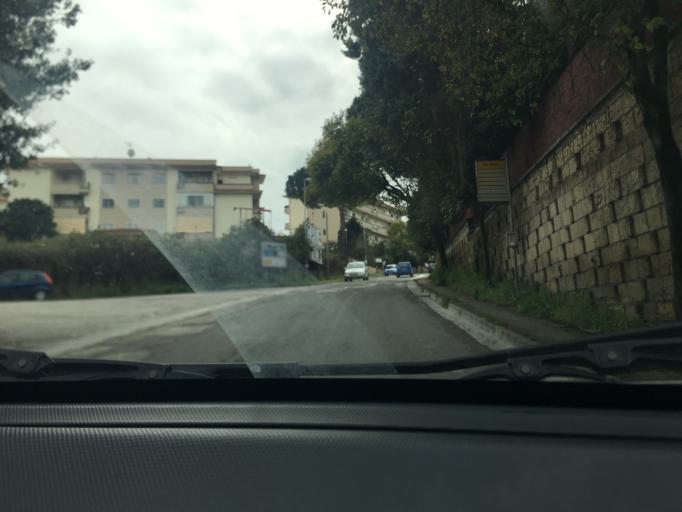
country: IT
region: Campania
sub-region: Provincia di Napoli
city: Marano di Napoli
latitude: 40.8935
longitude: 14.1811
